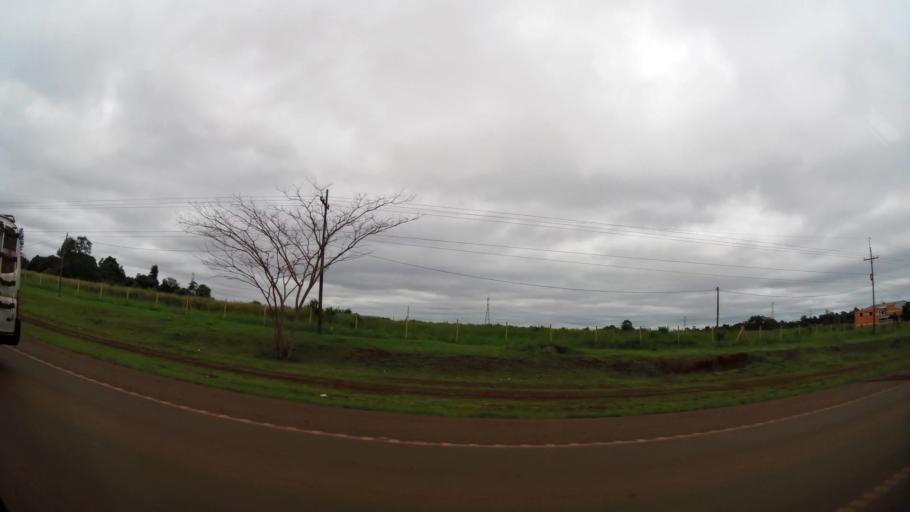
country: PY
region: Alto Parana
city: Colonia Yguazu
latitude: -25.4872
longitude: -54.8482
